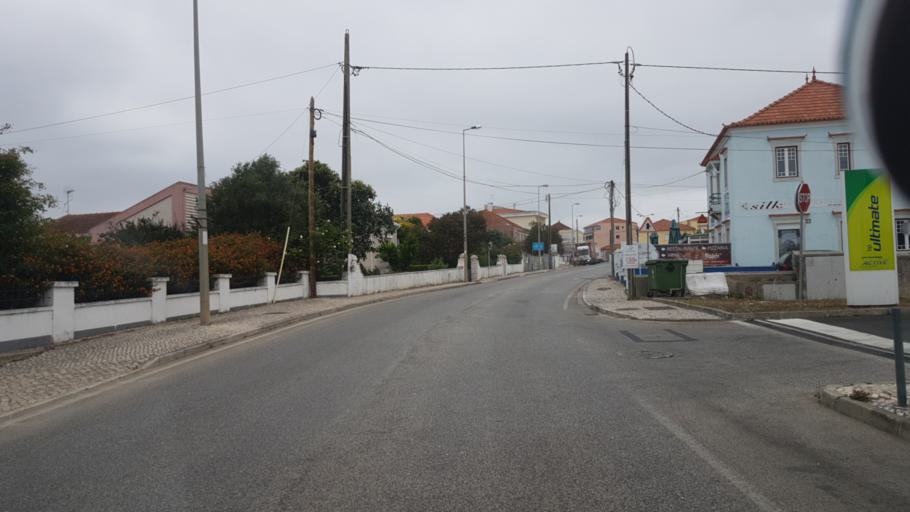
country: PT
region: Lisbon
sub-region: Sintra
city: Pero Pinheiro
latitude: 38.8526
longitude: -9.3266
